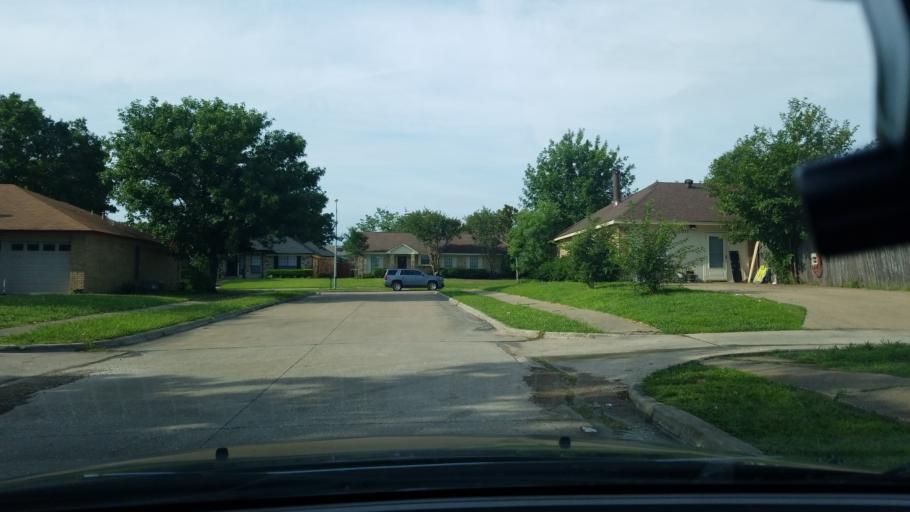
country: US
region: Texas
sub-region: Dallas County
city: Mesquite
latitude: 32.8009
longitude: -96.6134
